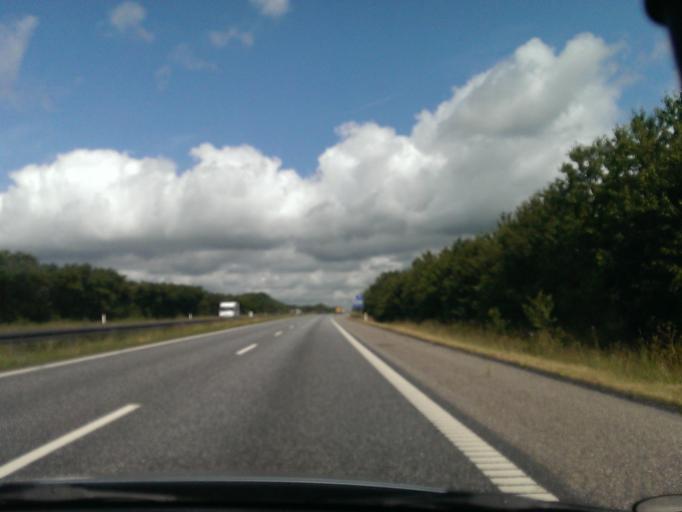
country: DK
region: North Denmark
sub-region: Mariagerfjord Kommune
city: Hobro
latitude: 56.7289
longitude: 9.7099
